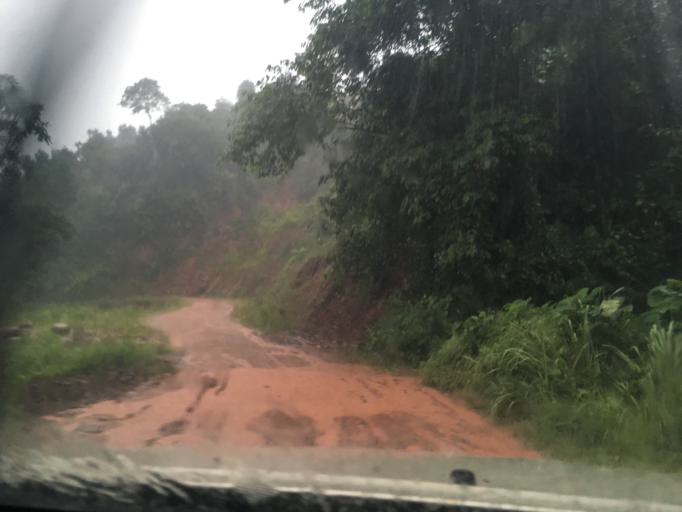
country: LA
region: Oudomxai
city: Muang La
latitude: 21.2312
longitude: 101.9612
